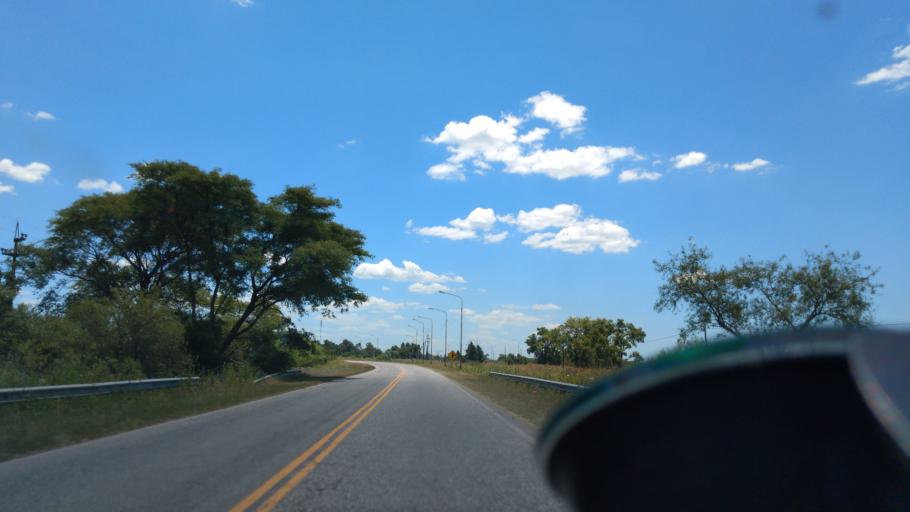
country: AR
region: Santa Fe
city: Laguna Paiva
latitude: -31.3291
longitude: -60.6595
